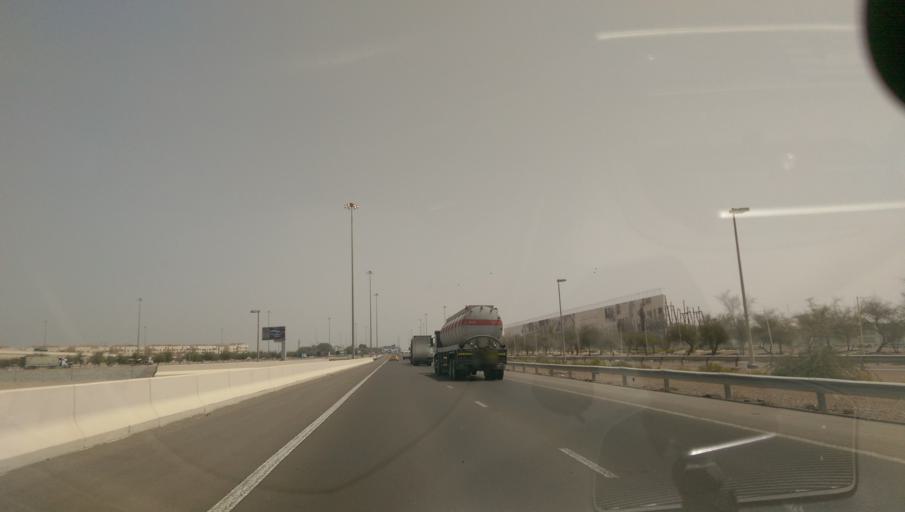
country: AE
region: Abu Dhabi
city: Abu Dhabi
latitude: 24.5438
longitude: 54.6940
